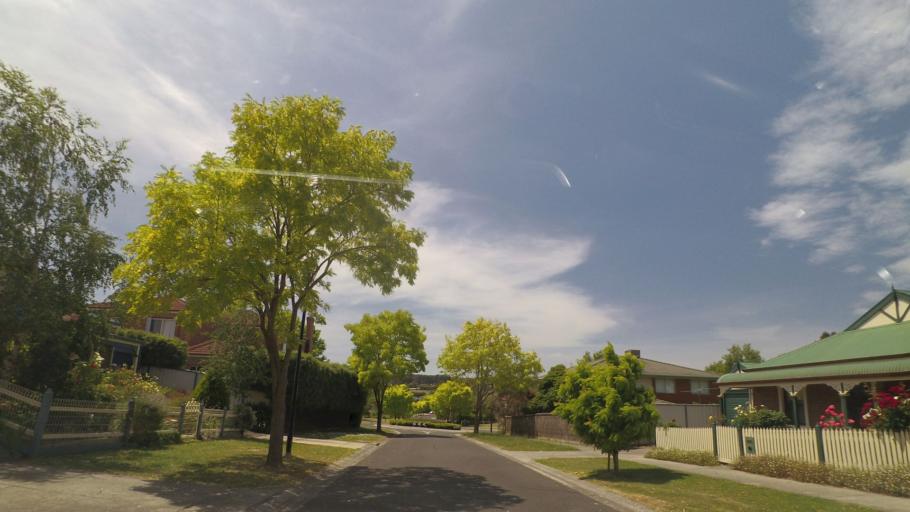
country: AU
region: Victoria
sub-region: Maroondah
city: Croydon North
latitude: -37.7594
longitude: 145.2984
